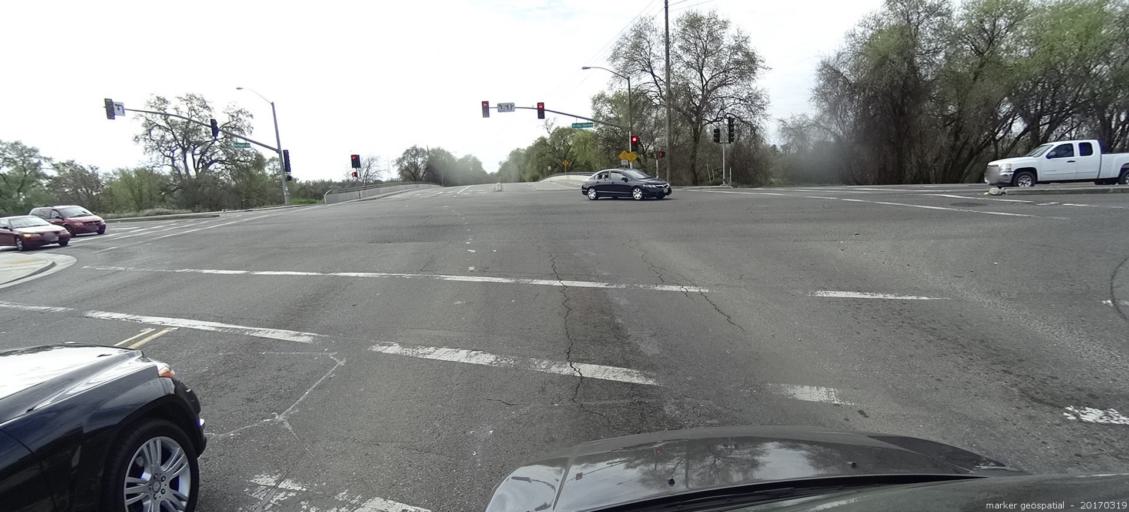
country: US
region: California
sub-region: Sacramento County
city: Sacramento
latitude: 38.6055
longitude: -121.4758
